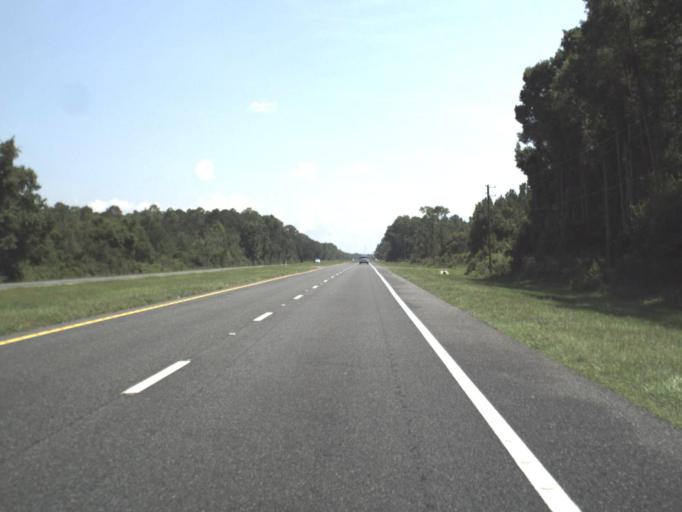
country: US
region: Florida
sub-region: Levy County
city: Inglis
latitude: 29.1546
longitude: -82.6387
